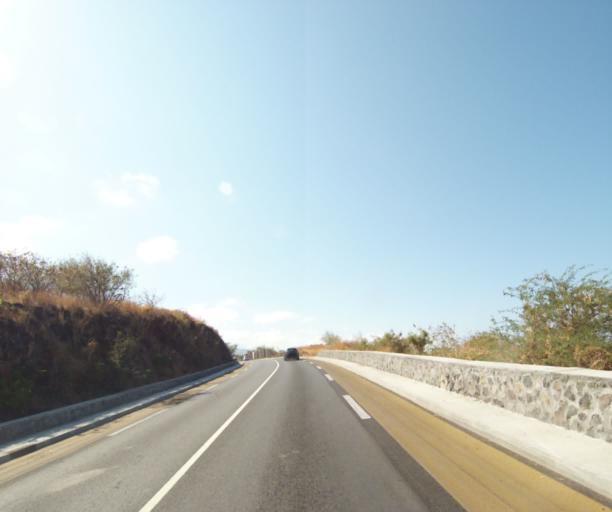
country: RE
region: Reunion
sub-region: Reunion
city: Trois-Bassins
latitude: -21.0931
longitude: 55.2436
